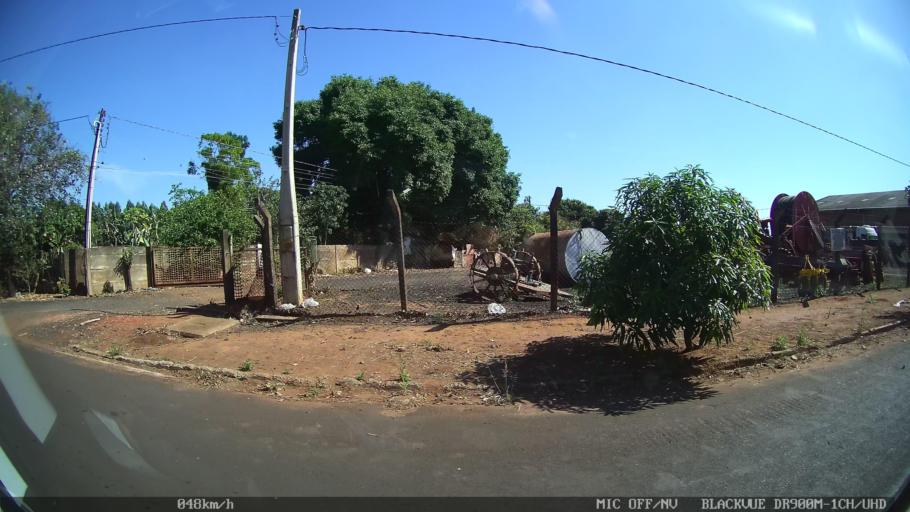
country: BR
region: Sao Paulo
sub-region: Batatais
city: Batatais
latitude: -20.8805
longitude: -47.6018
